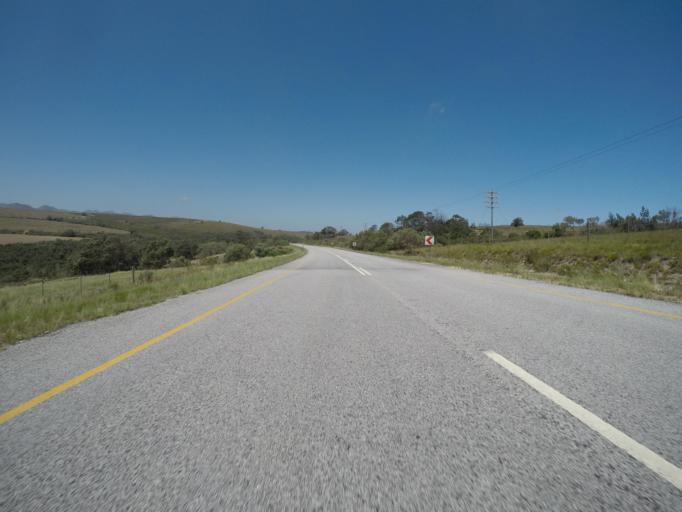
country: ZA
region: Eastern Cape
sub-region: Cacadu District Municipality
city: Kruisfontein
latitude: -34.0198
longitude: 24.5797
